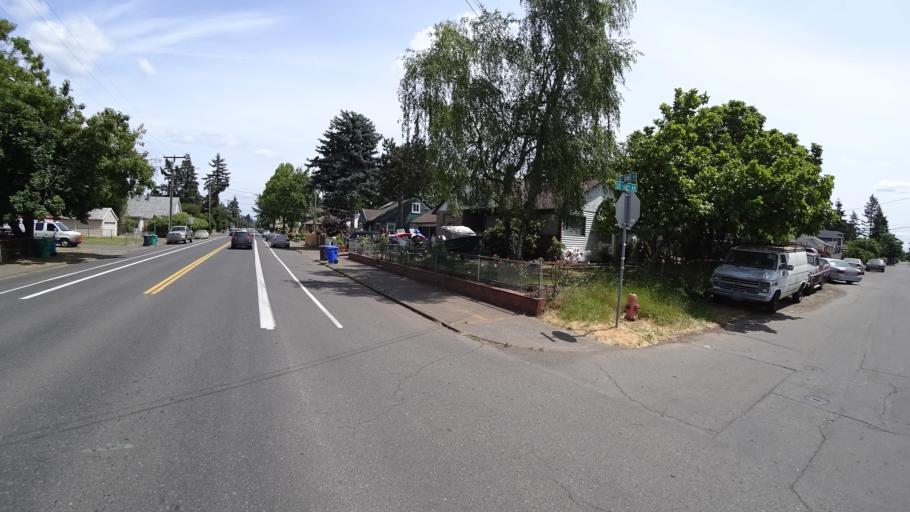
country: US
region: Oregon
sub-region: Multnomah County
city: Lents
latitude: 45.4758
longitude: -122.5971
